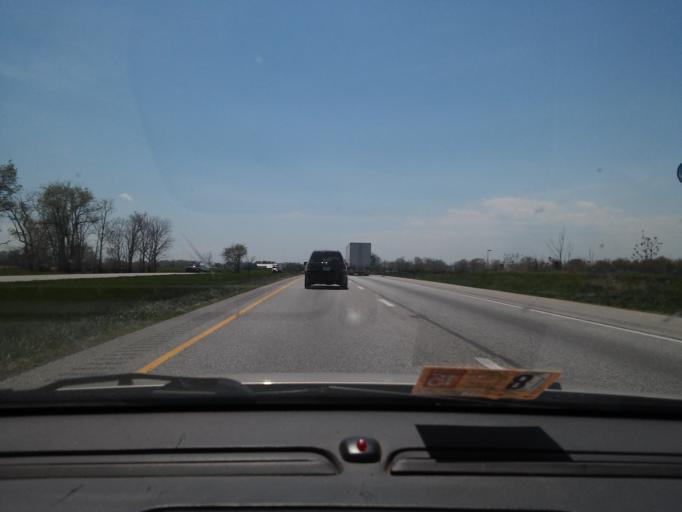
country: US
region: Pennsylvania
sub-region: Franklin County
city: Chambersburg
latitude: 39.8850
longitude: -77.6728
